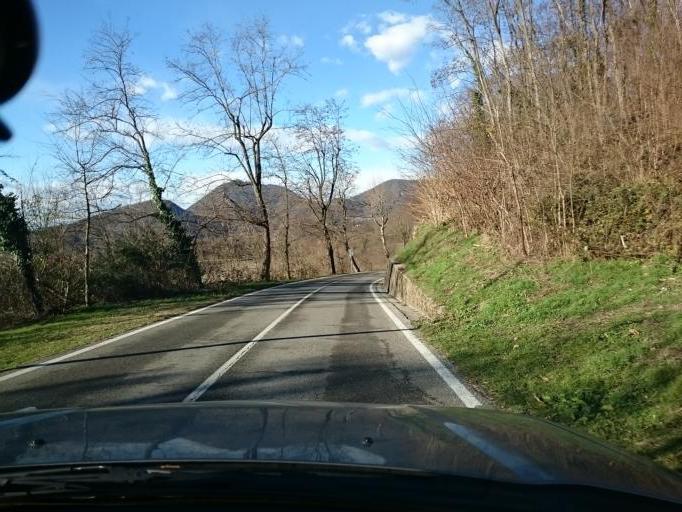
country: IT
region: Veneto
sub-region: Provincia di Padova
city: Vo
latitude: 45.3331
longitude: 11.6837
